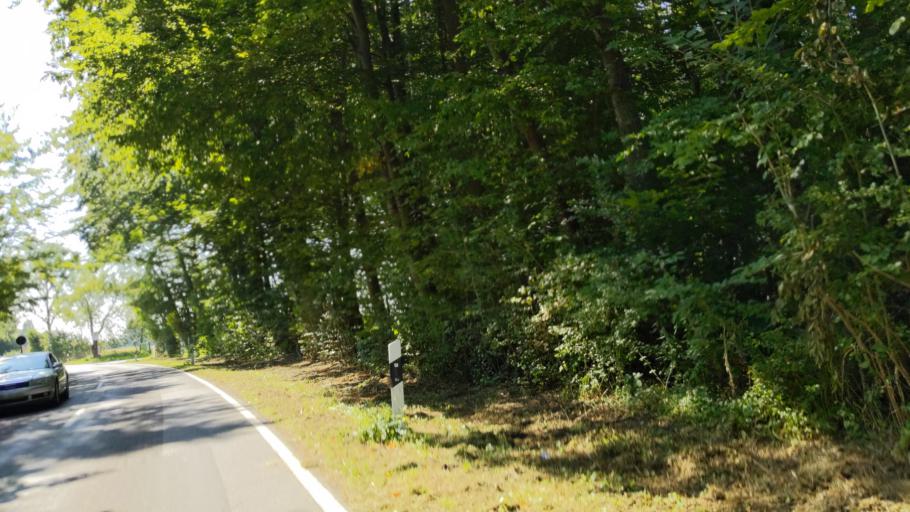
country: DE
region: Schleswig-Holstein
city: Hamberge
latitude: 53.8028
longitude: 10.6028
